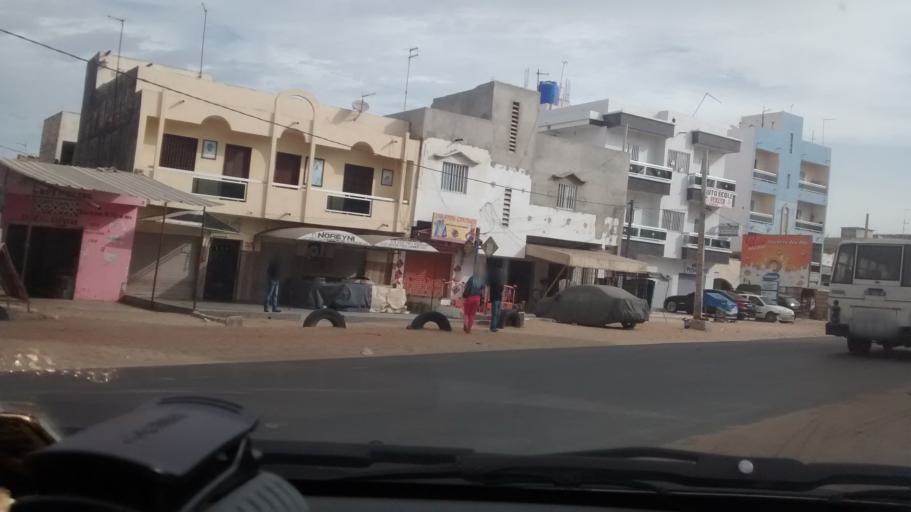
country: SN
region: Dakar
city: Pikine
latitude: 14.7652
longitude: -17.4175
